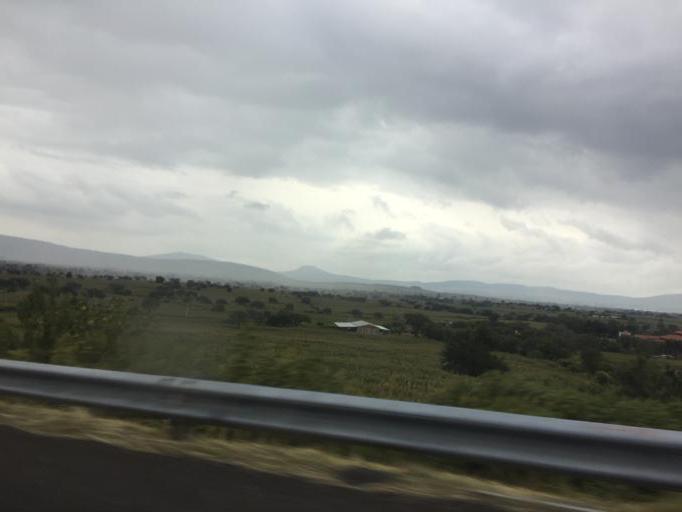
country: MX
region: Jalisco
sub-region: Zapotlan del Rey
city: Zapotlan del Rey
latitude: 20.4703
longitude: -102.9151
